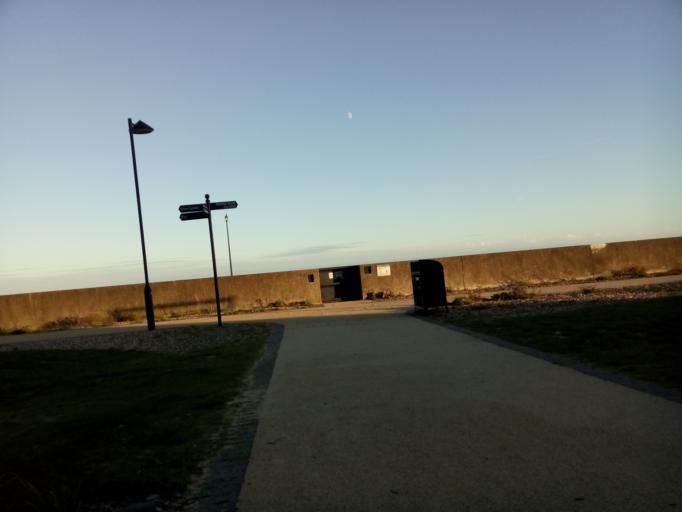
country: GB
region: England
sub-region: Suffolk
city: Felixstowe
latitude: 51.9498
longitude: 1.3362
